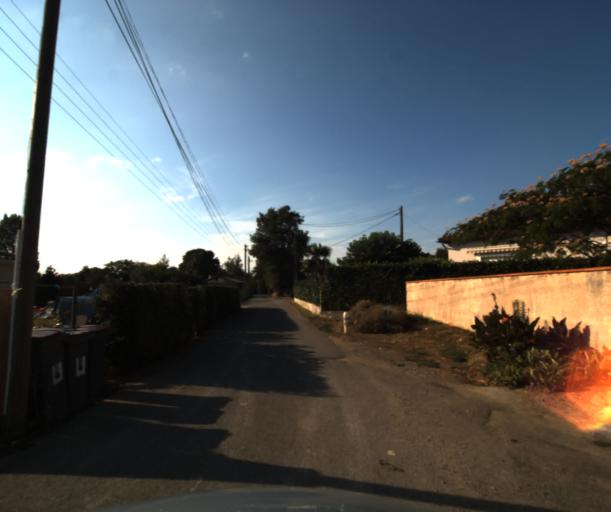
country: FR
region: Midi-Pyrenees
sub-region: Departement de la Haute-Garonne
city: Saint-Lys
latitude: 43.5036
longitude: 1.1867
